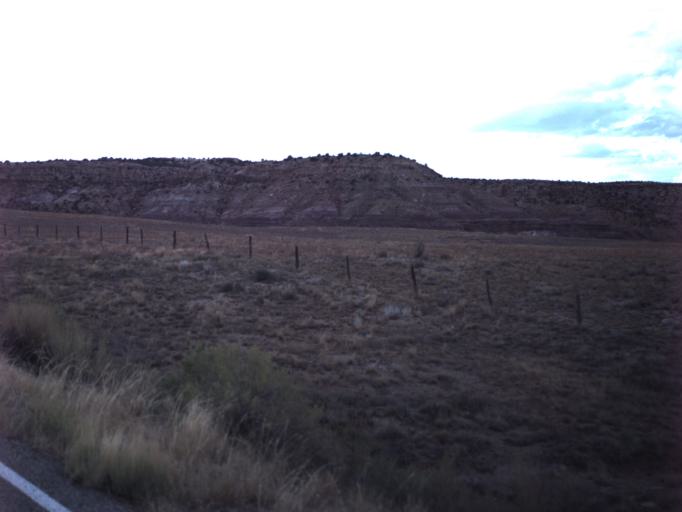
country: US
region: Utah
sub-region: San Juan County
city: Blanding
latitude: 37.4203
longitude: -109.4591
